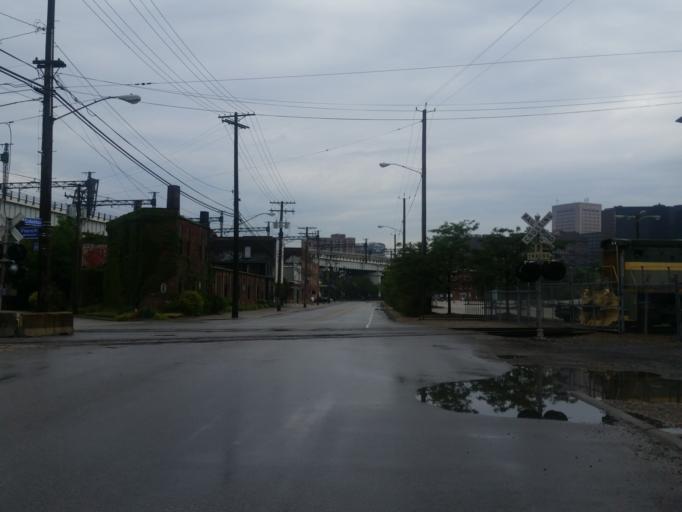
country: US
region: Ohio
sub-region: Cuyahoga County
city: Cleveland
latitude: 41.4916
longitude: -81.7004
